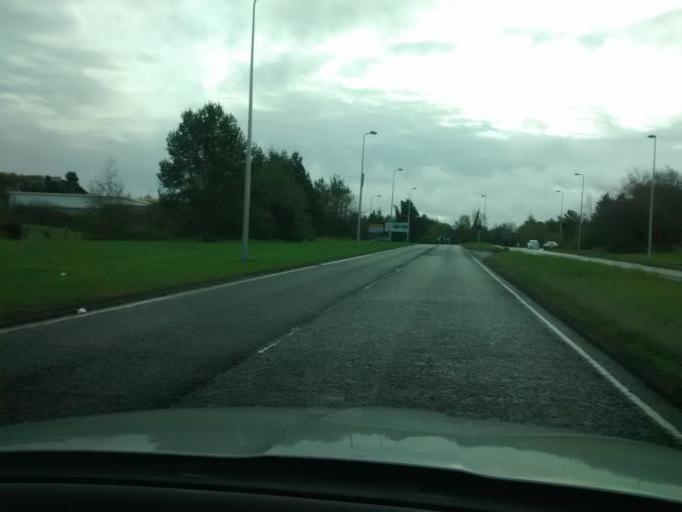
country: GB
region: Scotland
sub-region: West Lothian
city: Mid Calder
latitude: 55.8820
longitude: -3.4934
